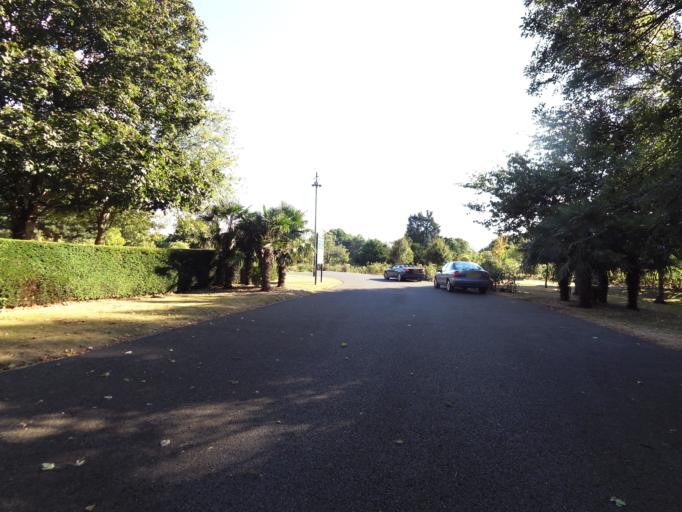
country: GB
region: England
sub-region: Greater London
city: Harringay
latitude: 51.6050
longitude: -0.0818
